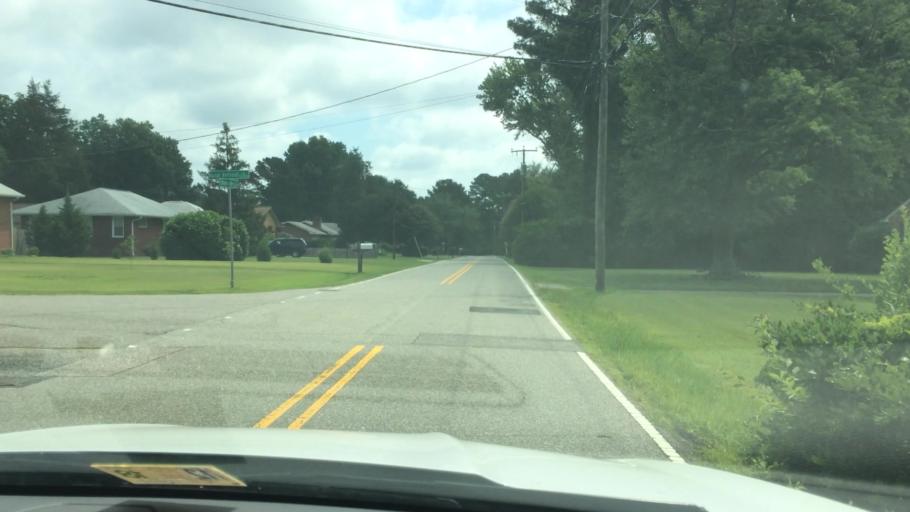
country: US
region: Virginia
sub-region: City of Poquoson
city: Poquoson
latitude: 37.1381
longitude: -76.4506
